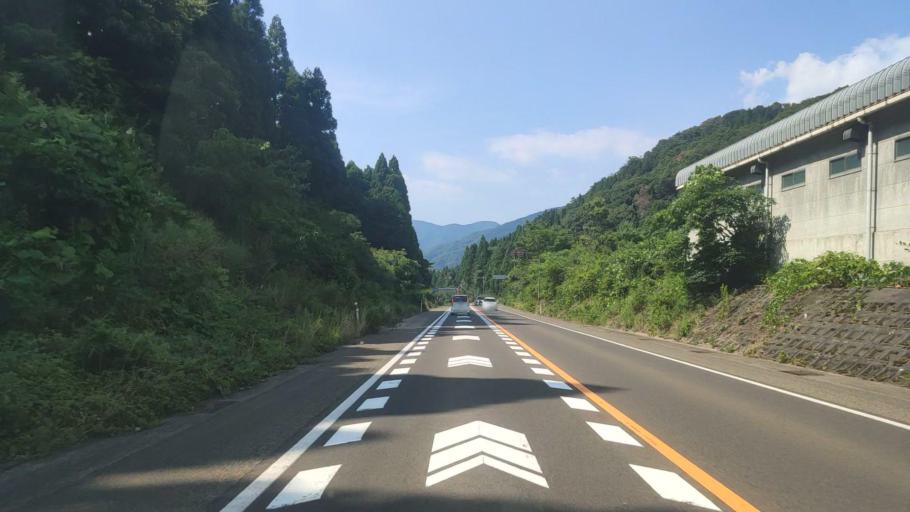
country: JP
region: Fukui
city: Tsuruga
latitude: 35.5898
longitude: 136.1241
